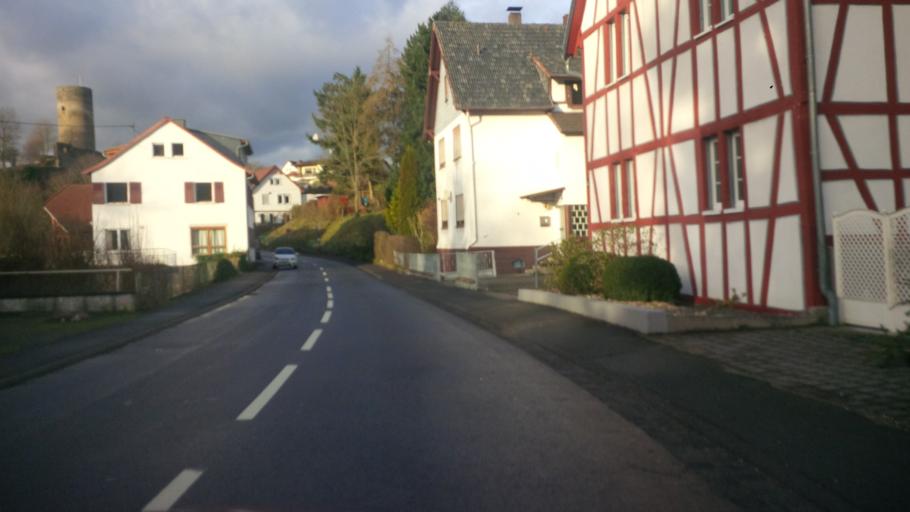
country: DE
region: Hesse
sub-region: Regierungsbezirk Darmstadt
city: Schmitten
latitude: 50.3159
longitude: 8.4236
